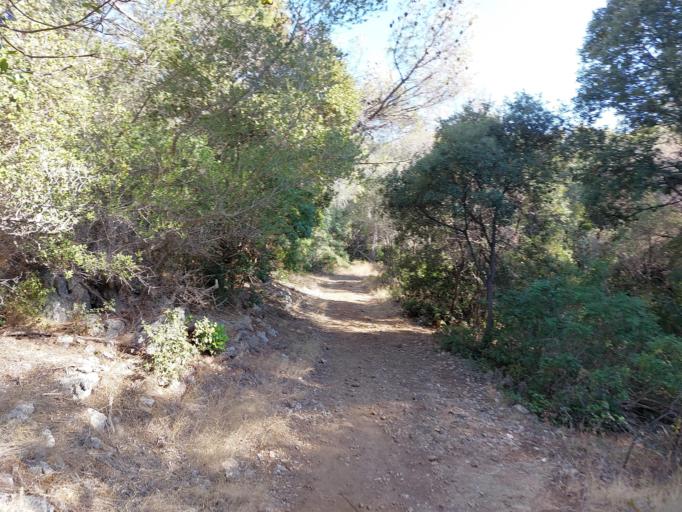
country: HR
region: Dubrovacko-Neretvanska
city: Smokvica
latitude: 42.7590
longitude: 16.8082
